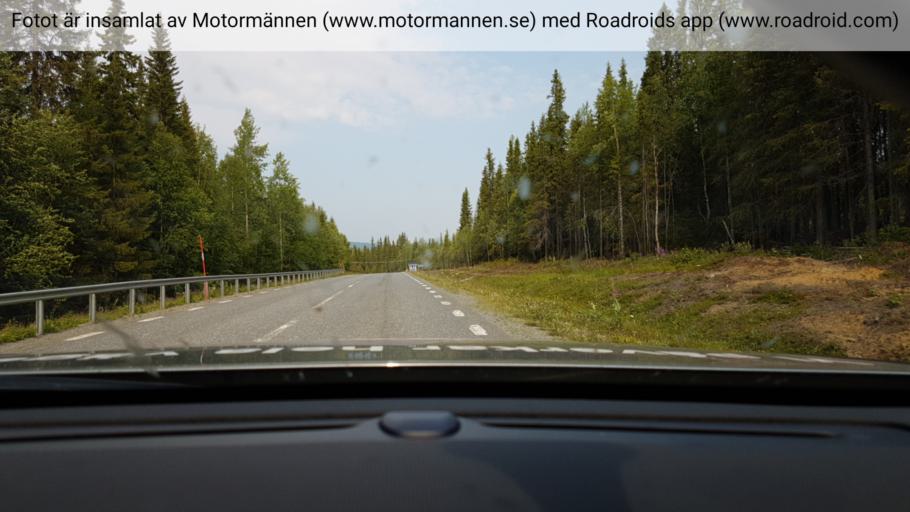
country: SE
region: Vaesterbotten
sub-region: Vilhelmina Kommun
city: Sjoberg
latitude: 65.4830
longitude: 15.9664
